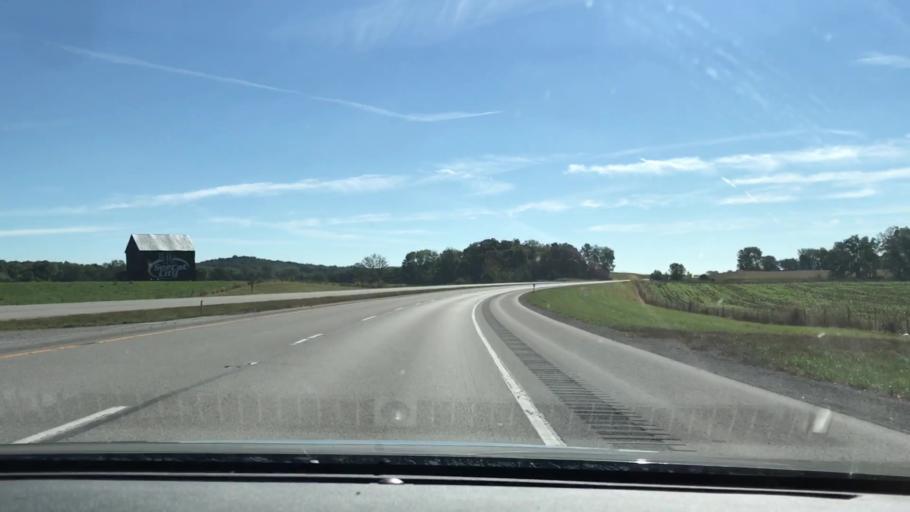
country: US
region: Kentucky
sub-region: Todd County
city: Elkton
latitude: 36.8228
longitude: -87.1476
